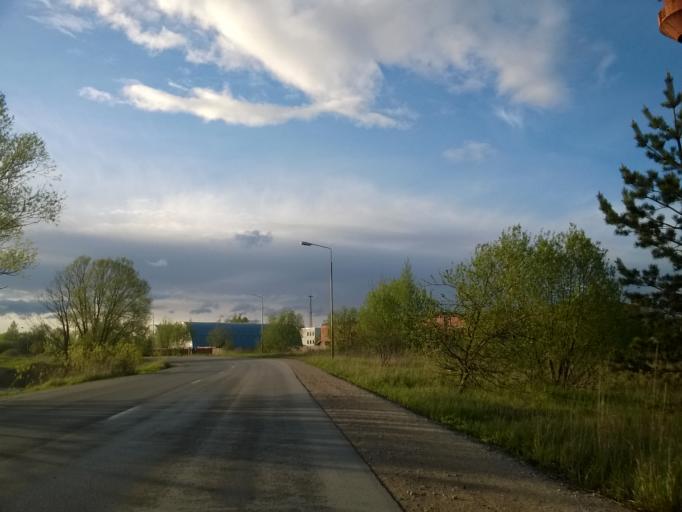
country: LV
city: Tireli
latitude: 56.9367
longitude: 23.6026
